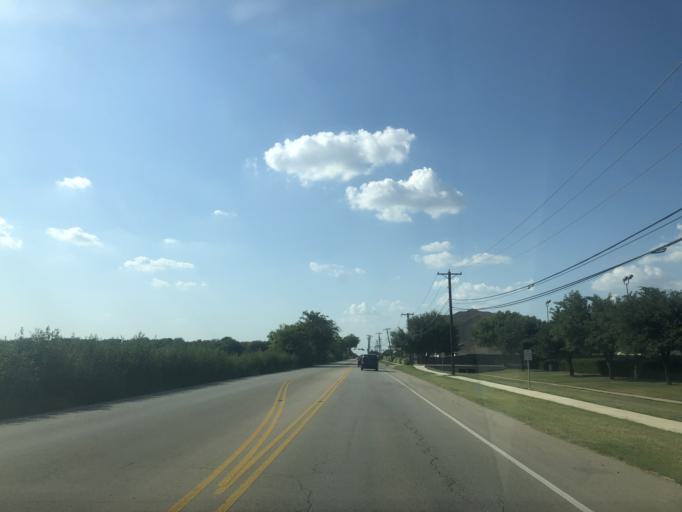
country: US
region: Texas
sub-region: Tarrant County
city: Saginaw
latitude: 32.8444
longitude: -97.3840
